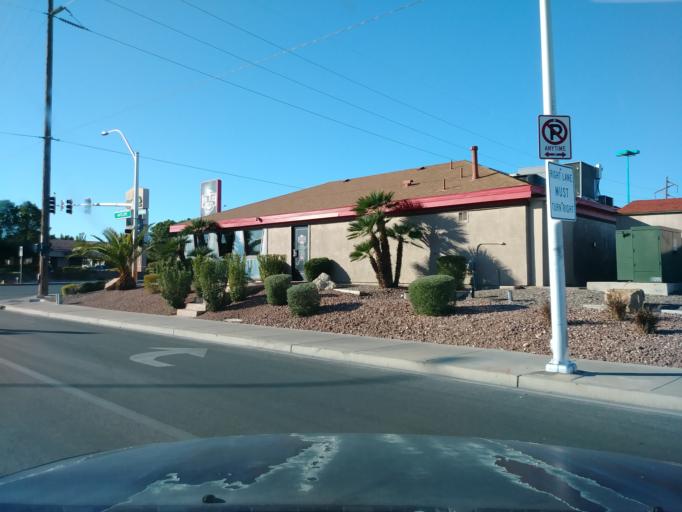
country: US
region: Nevada
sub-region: Clark County
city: Spring Valley
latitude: 36.1596
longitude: -115.2510
